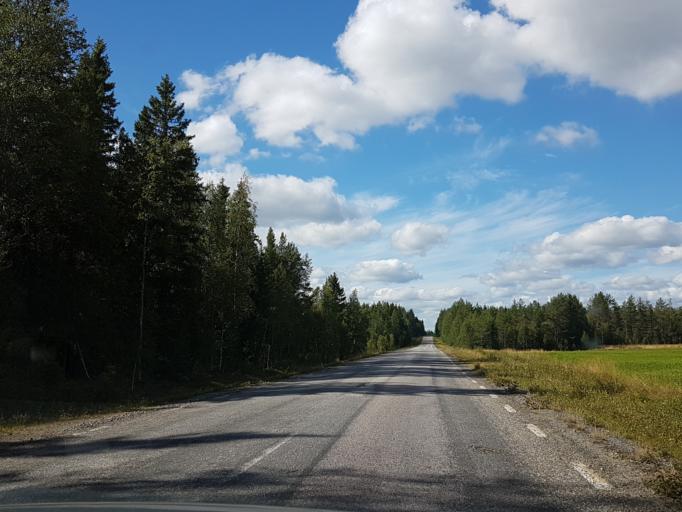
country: SE
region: Vaesterbotten
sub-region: Umea Kommun
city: Saevar
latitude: 64.2066
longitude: 20.4972
